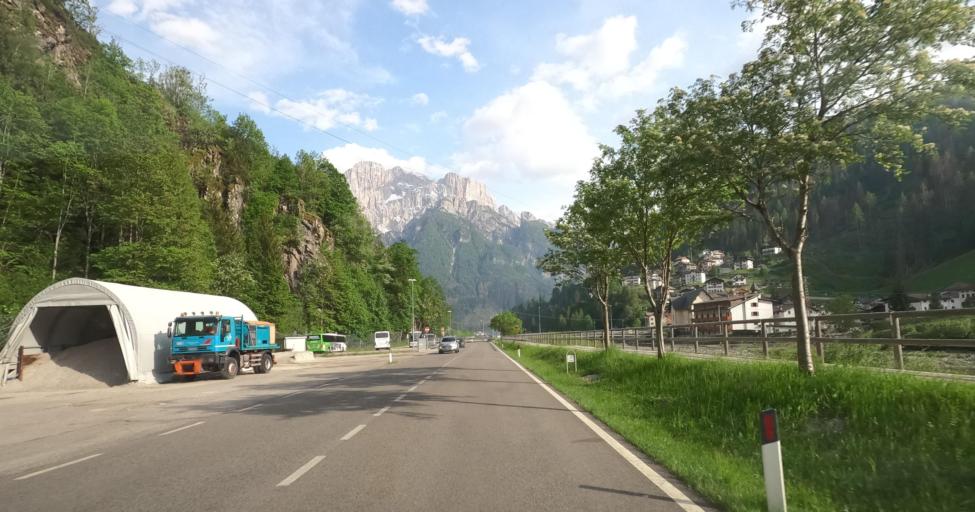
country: IT
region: Veneto
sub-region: Provincia di Belluno
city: Alleghe
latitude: 46.4238
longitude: 12.0083
